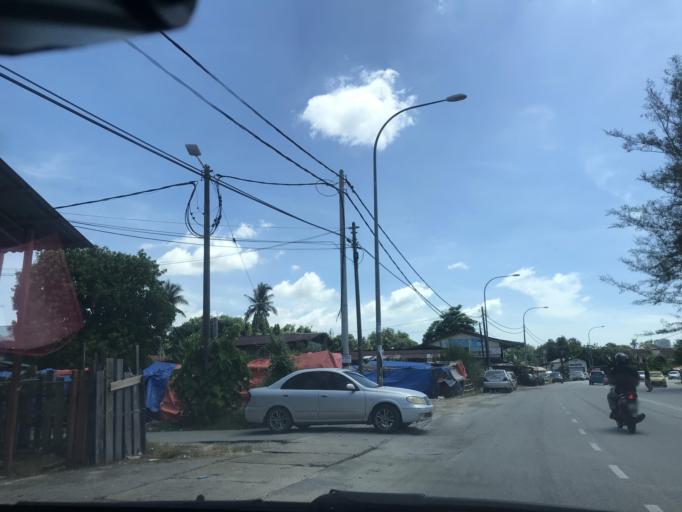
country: MY
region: Kelantan
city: Kota Bharu
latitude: 6.1102
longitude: 102.2632
